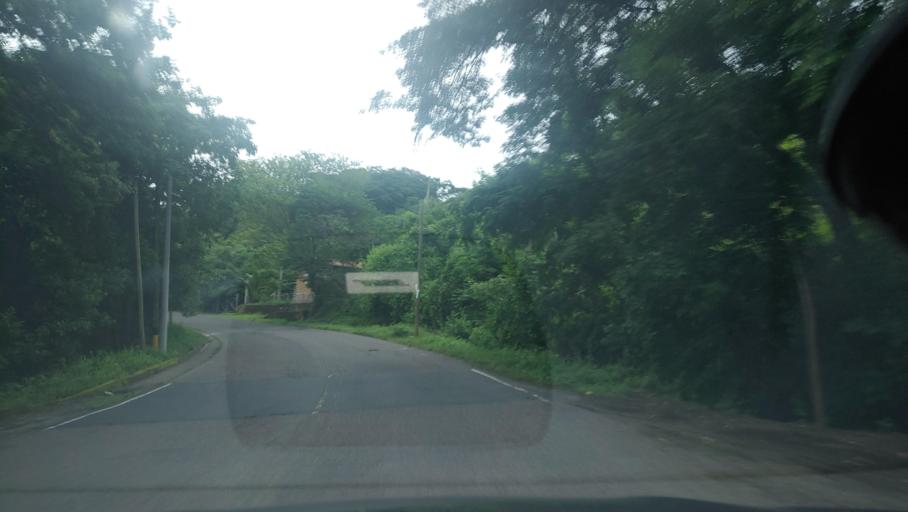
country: HN
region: Choluteca
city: Corpus
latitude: 13.3710
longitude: -87.0417
